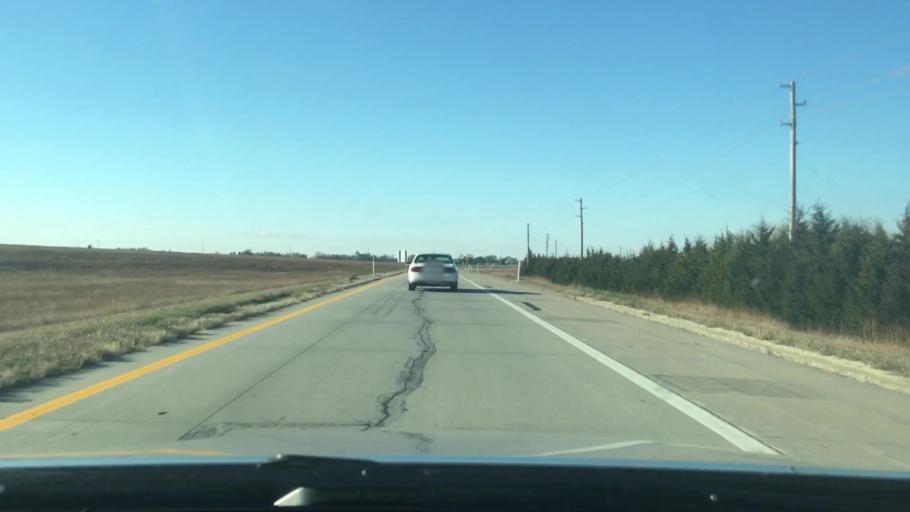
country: US
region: Kansas
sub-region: Reno County
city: South Hutchinson
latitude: 38.0157
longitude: -97.9658
